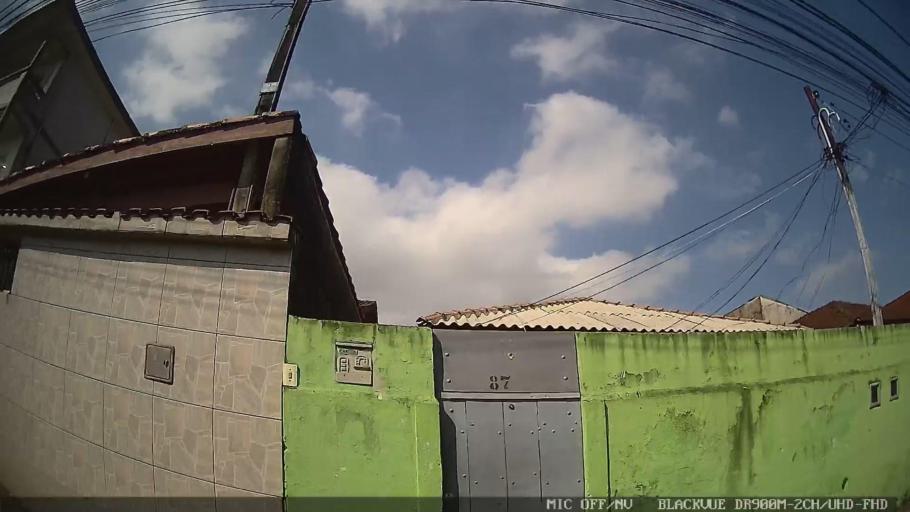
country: BR
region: Sao Paulo
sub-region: Santos
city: Santos
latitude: -23.9416
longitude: -46.3052
